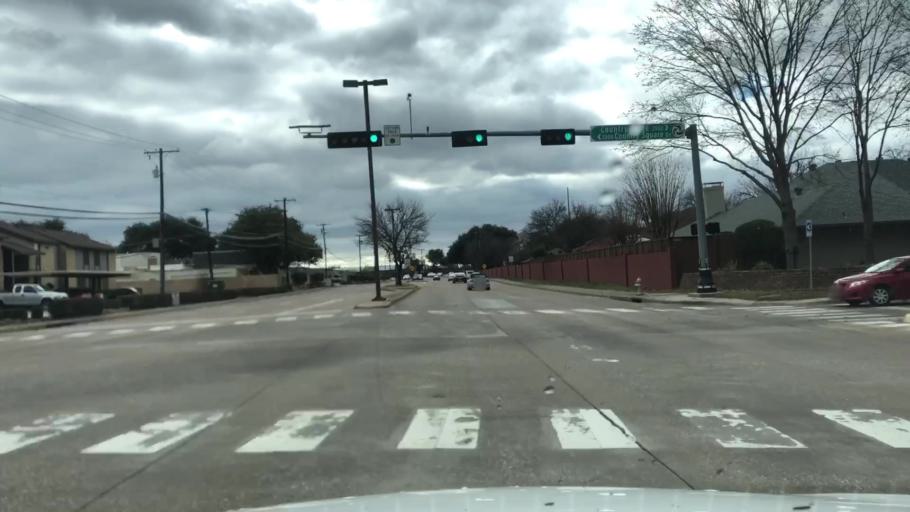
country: US
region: Texas
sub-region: Dallas County
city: Addison
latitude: 32.9605
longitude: -96.8538
